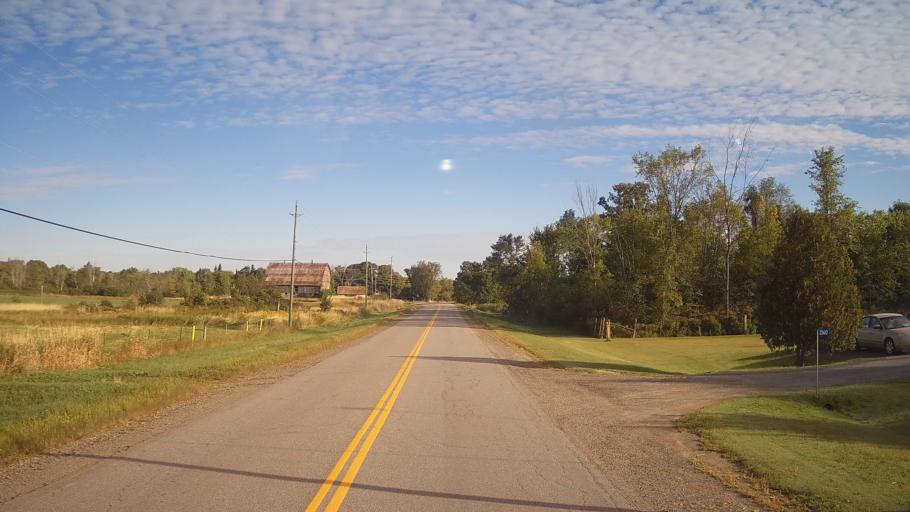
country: CA
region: Ontario
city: Gananoque
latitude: 44.3813
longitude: -76.1379
